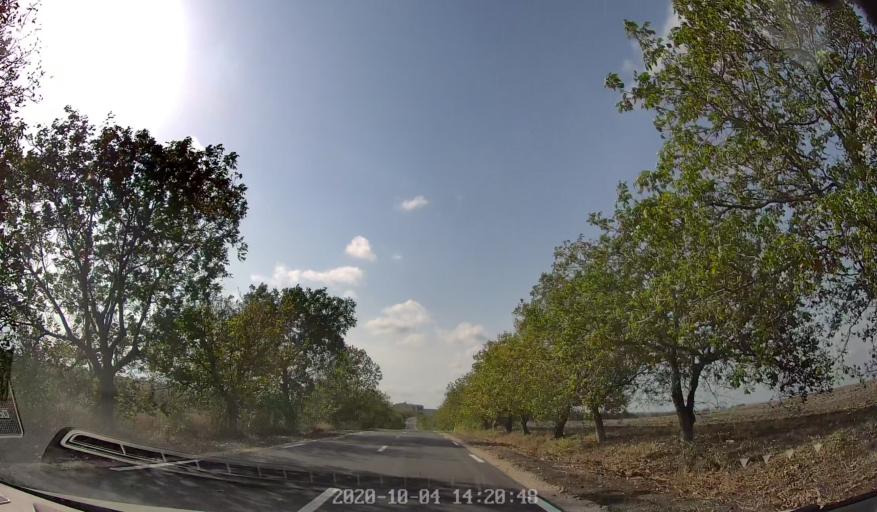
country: MD
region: Rezina
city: Saharna
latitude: 47.5839
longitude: 28.9636
